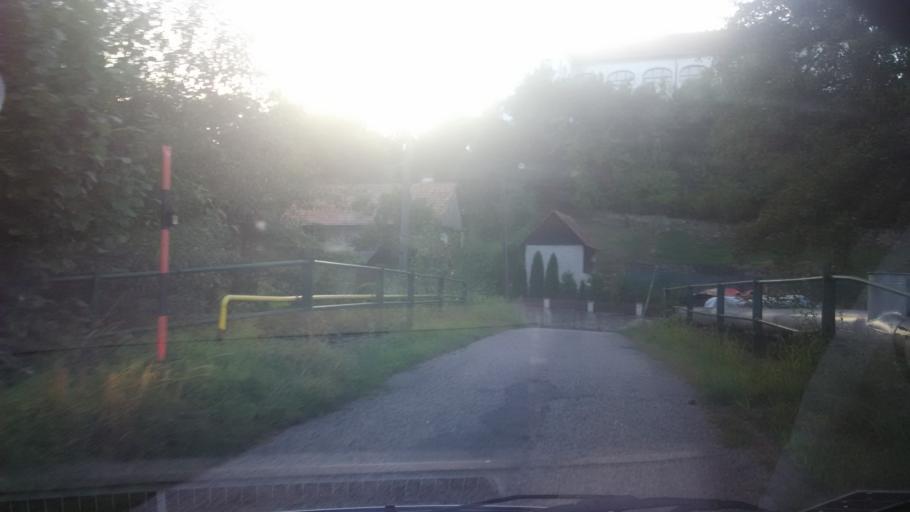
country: SK
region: Banskobystricky
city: Dudince
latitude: 48.2982
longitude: 18.7746
